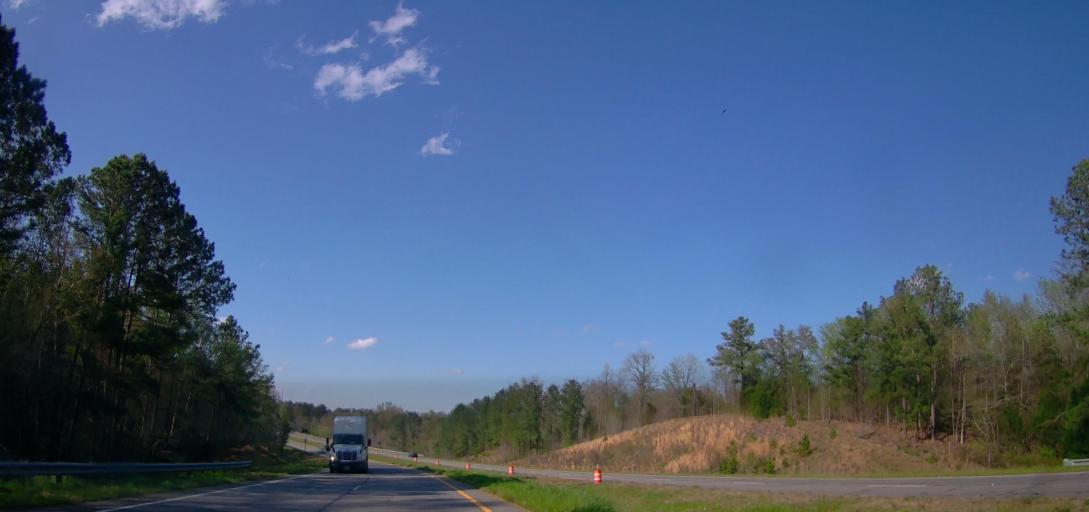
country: US
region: Georgia
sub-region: Baldwin County
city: Milledgeville
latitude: 33.0679
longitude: -83.2491
